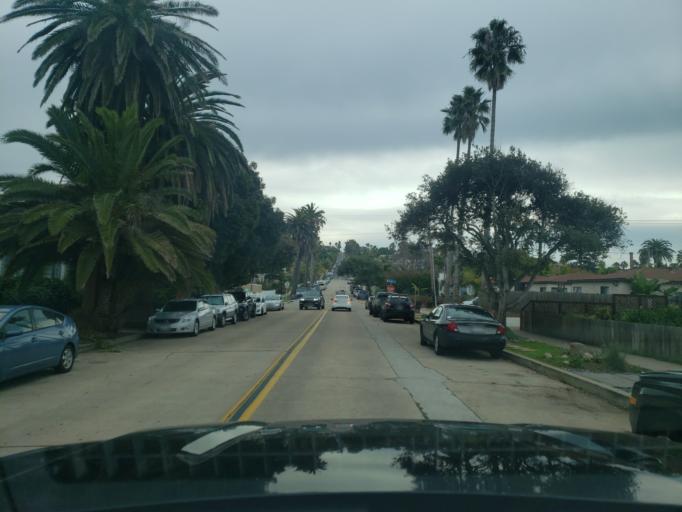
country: US
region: California
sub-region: San Diego County
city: Coronado
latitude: 32.7419
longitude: -117.2536
